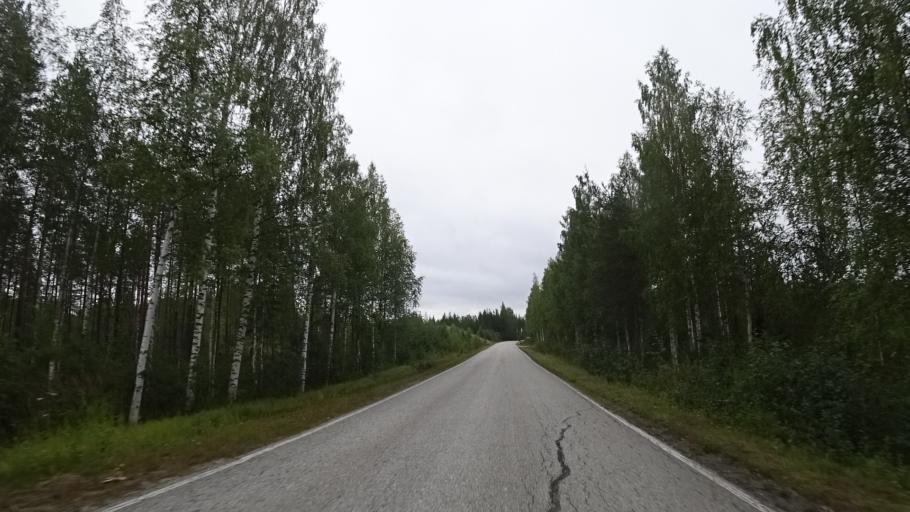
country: FI
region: North Karelia
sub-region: Pielisen Karjala
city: Lieksa
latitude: 63.3533
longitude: 30.2640
